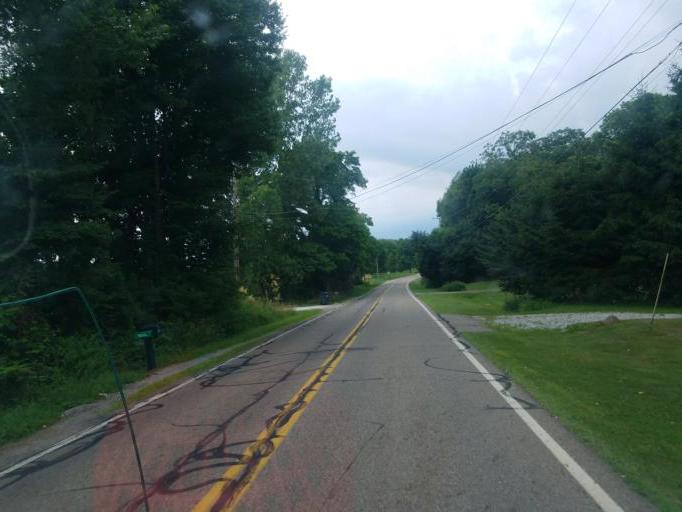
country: US
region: Ohio
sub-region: Stark County
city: Hartville
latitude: 41.0288
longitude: -81.2909
